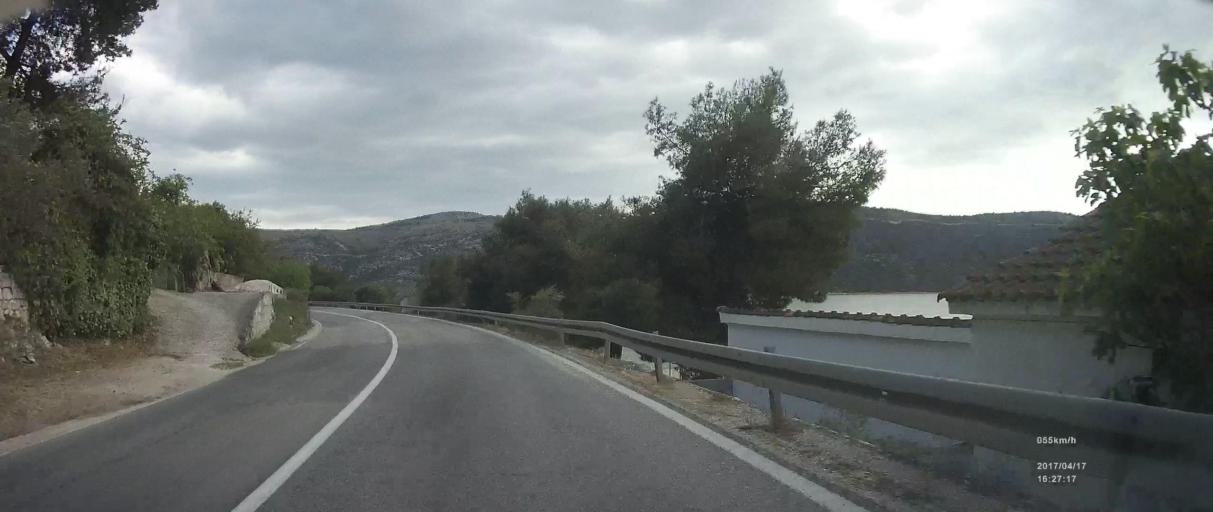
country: HR
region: Splitsko-Dalmatinska
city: Veliki Drvenik
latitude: 43.5168
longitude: 16.1424
